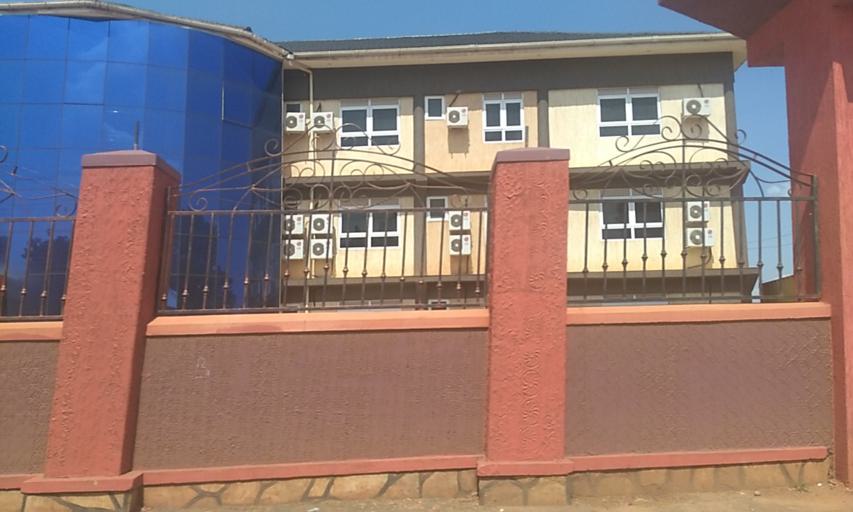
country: UG
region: Central Region
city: Kampala Central Division
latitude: 0.3816
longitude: 32.5965
